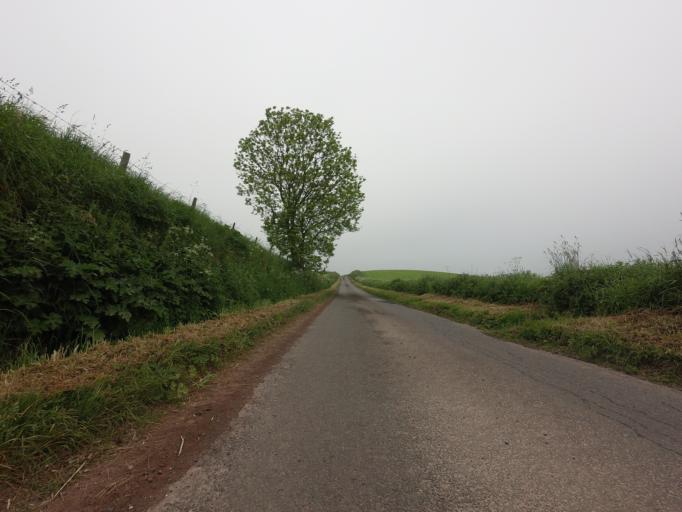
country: GB
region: Scotland
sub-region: Perth and Kinross
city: Abernethy
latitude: 56.2641
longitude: -3.3048
